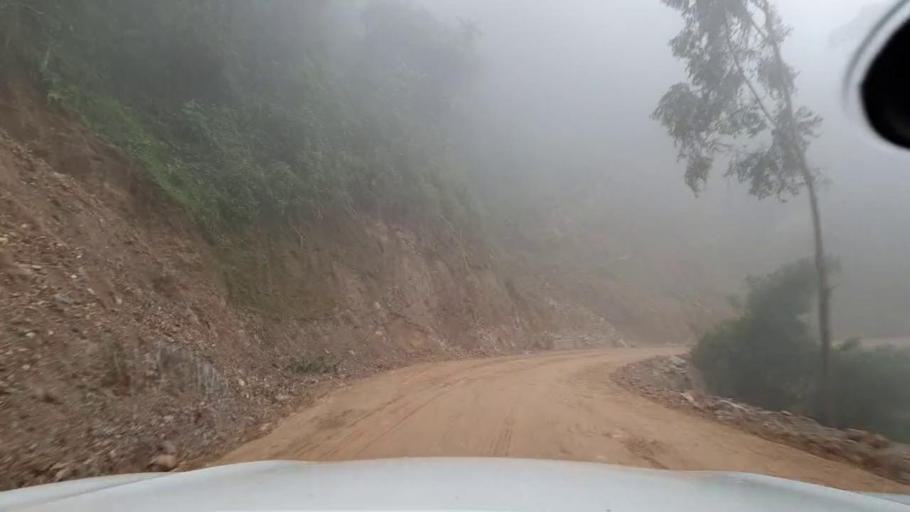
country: RW
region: Western Province
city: Cyangugu
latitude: -2.5903
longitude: 29.1911
